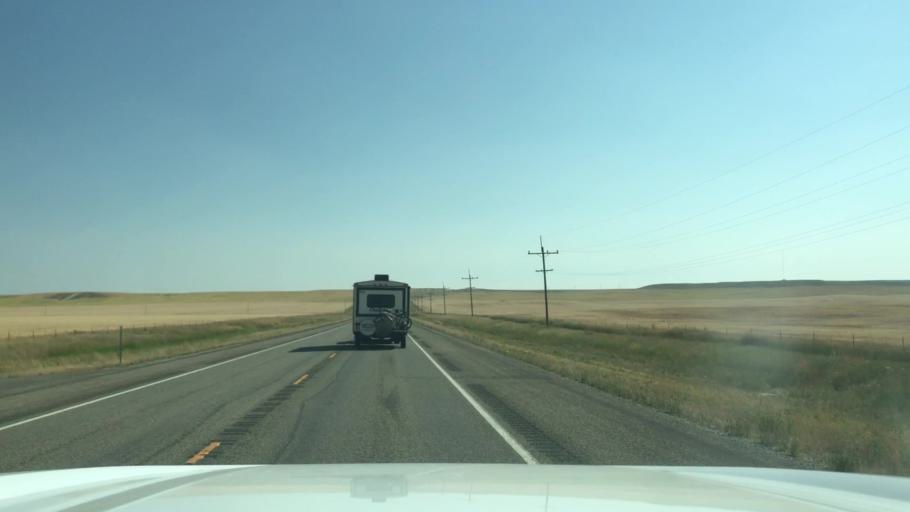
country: US
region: Montana
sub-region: Wheatland County
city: Harlowton
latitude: 46.4856
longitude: -109.7661
